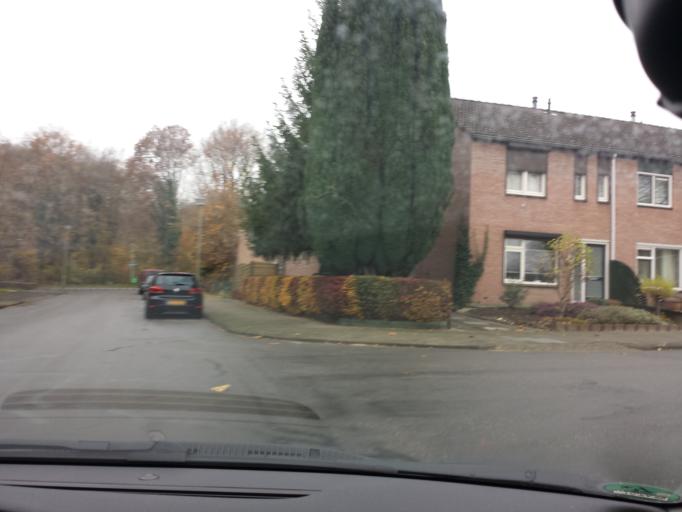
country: NL
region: Limburg
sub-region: Gemeente Kerkrade
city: Kerkrade
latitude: 50.8971
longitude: 6.0561
